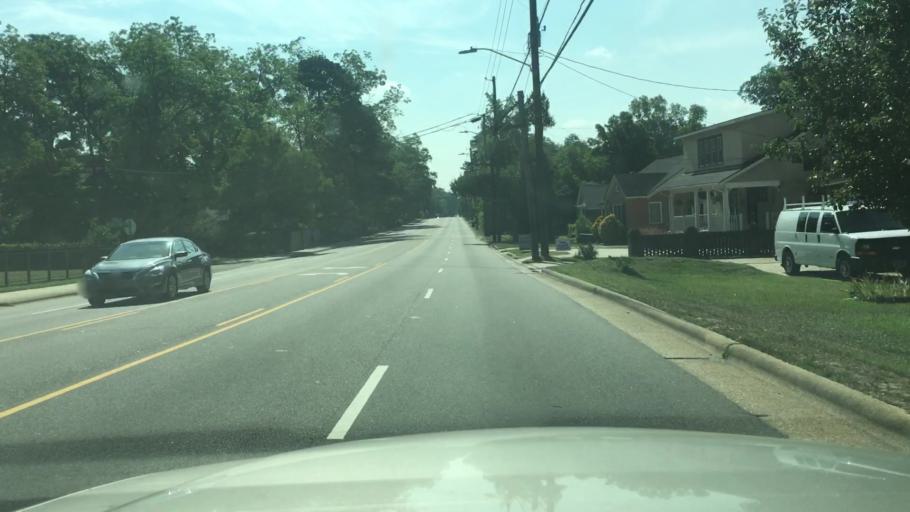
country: US
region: North Carolina
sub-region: Cumberland County
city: Fayetteville
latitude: 35.0603
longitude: -78.9146
